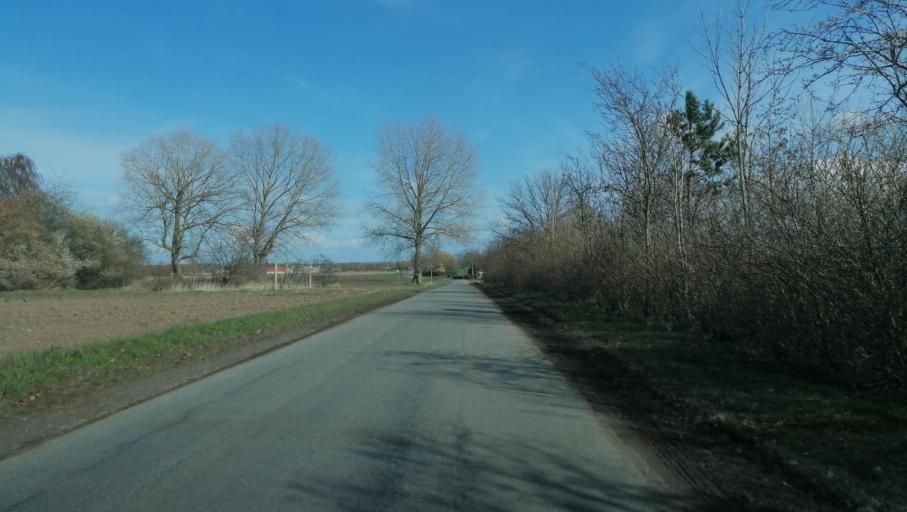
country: DK
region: Zealand
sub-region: Odsherred Kommune
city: Horve
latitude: 55.7482
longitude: 11.4683
